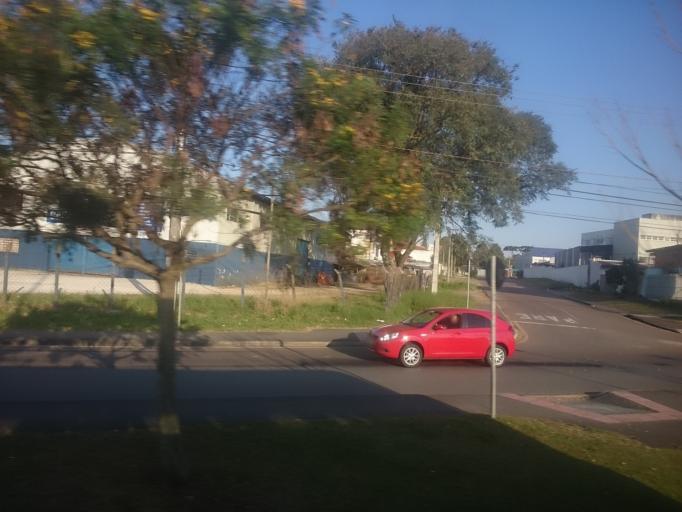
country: BR
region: Parana
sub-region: Curitiba
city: Curitiba
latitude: -25.4818
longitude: -49.2638
